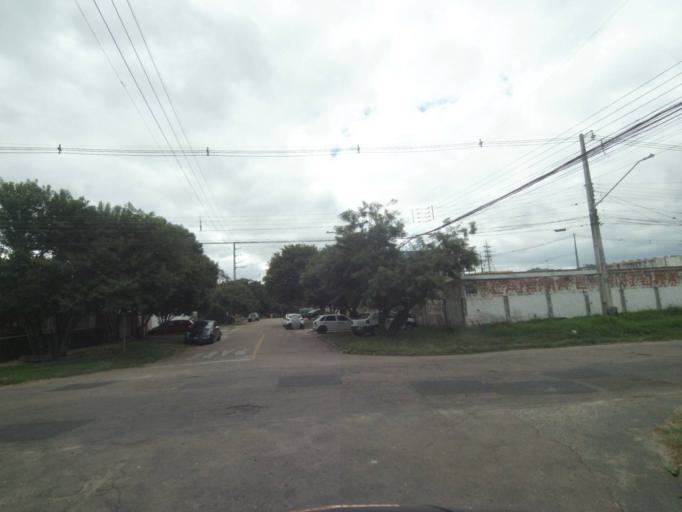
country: BR
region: Parana
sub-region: Sao Jose Dos Pinhais
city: Sao Jose dos Pinhais
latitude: -25.5517
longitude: -49.2553
